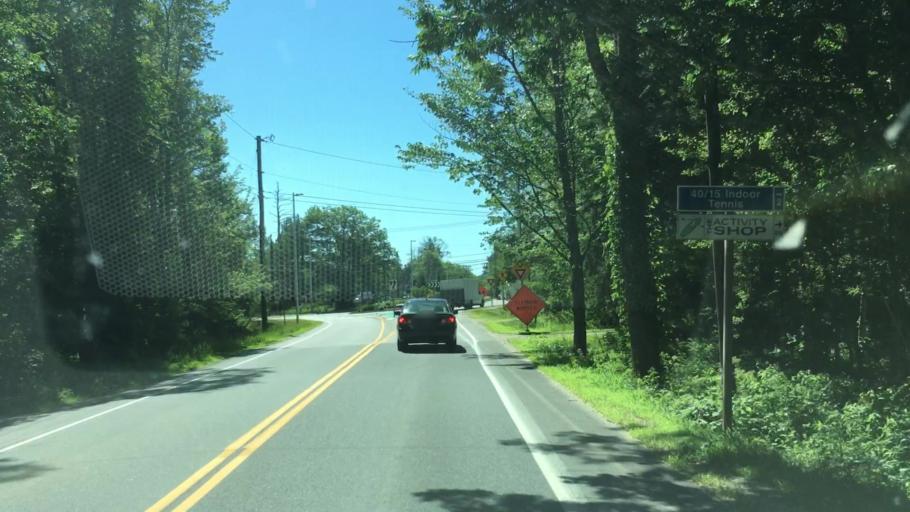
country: US
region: Maine
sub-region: Hancock County
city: Sedgwick
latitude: 44.4088
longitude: -68.5986
